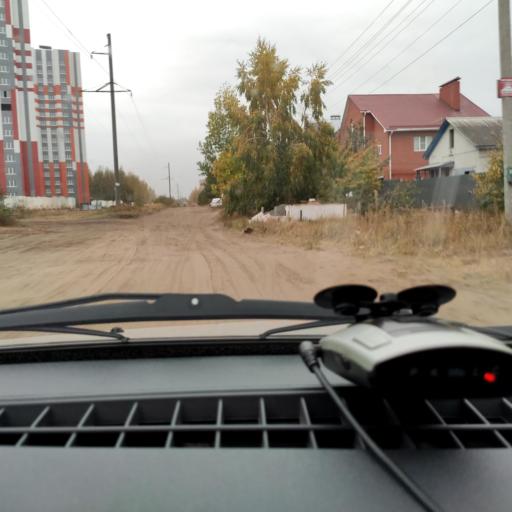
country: RU
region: Voronezj
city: Podgornoye
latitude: 51.7613
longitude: 39.1771
